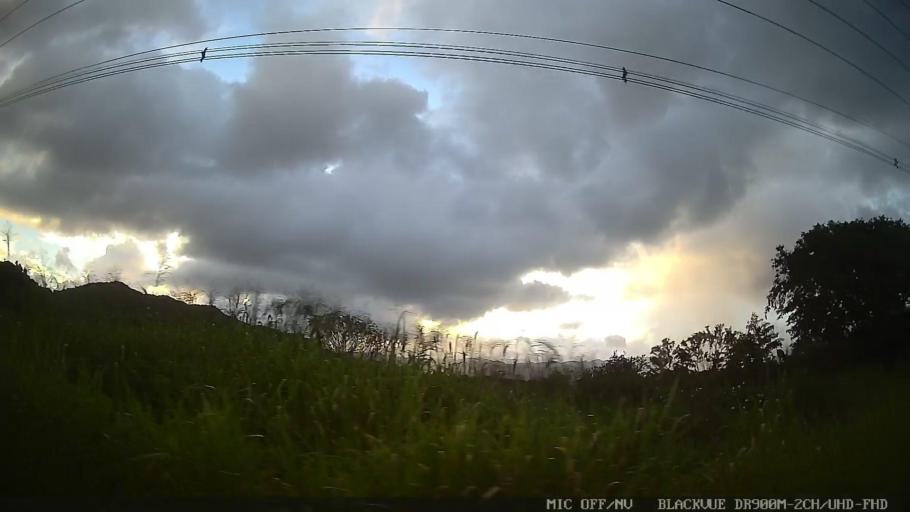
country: BR
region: Sao Paulo
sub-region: Itanhaem
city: Itanhaem
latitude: -24.0976
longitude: -46.8012
